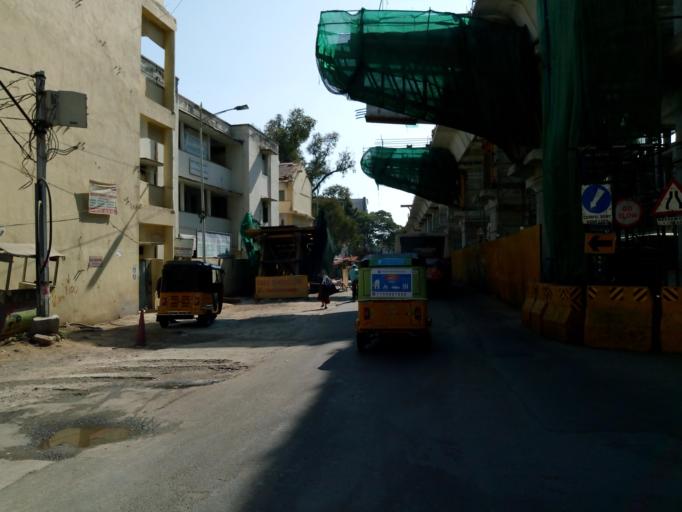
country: IN
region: Telangana
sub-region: Hyderabad
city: Hyderabad
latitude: 17.3950
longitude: 78.4902
